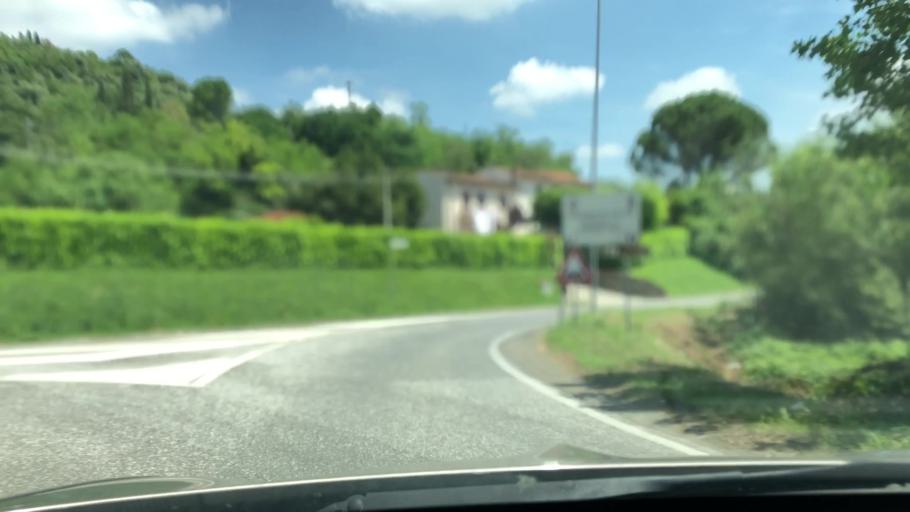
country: IT
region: Tuscany
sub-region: Province of Pisa
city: Forcoli
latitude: 43.6093
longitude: 10.6903
